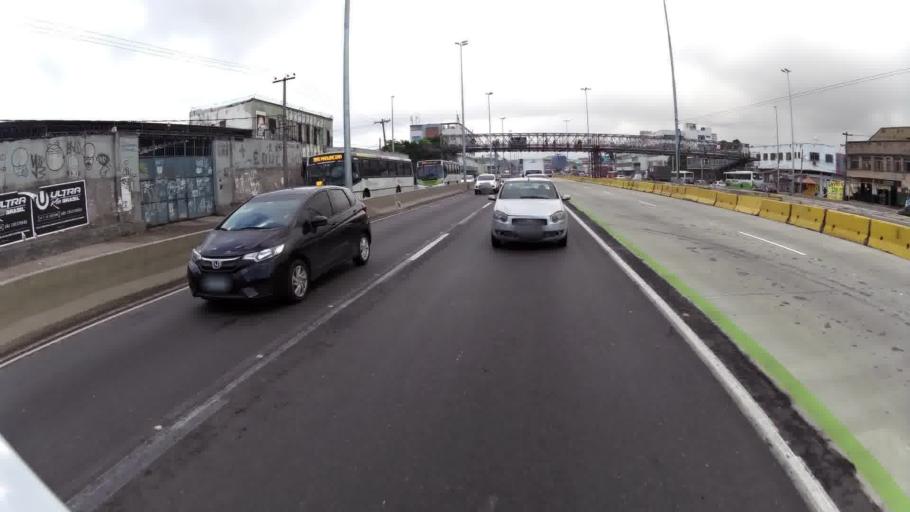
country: BR
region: Rio de Janeiro
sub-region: Rio De Janeiro
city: Rio de Janeiro
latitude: -22.8600
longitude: -43.2477
